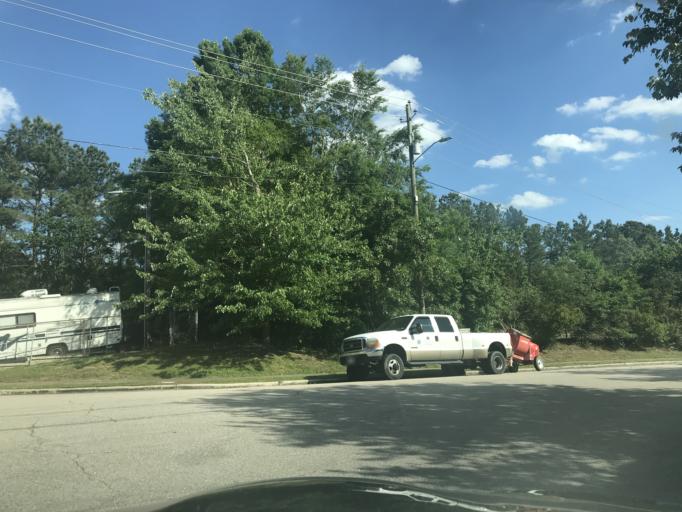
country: US
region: North Carolina
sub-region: Wake County
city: Raleigh
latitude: 35.8587
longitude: -78.5990
